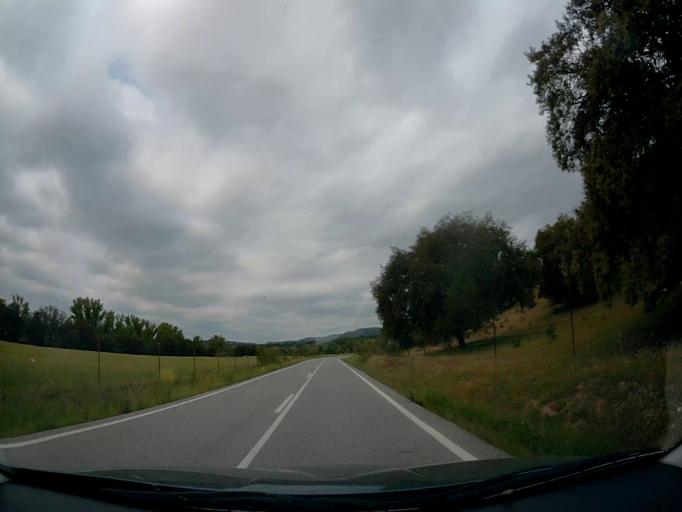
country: ES
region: Madrid
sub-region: Provincia de Madrid
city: Quijorna
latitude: 40.4200
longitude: -4.0877
